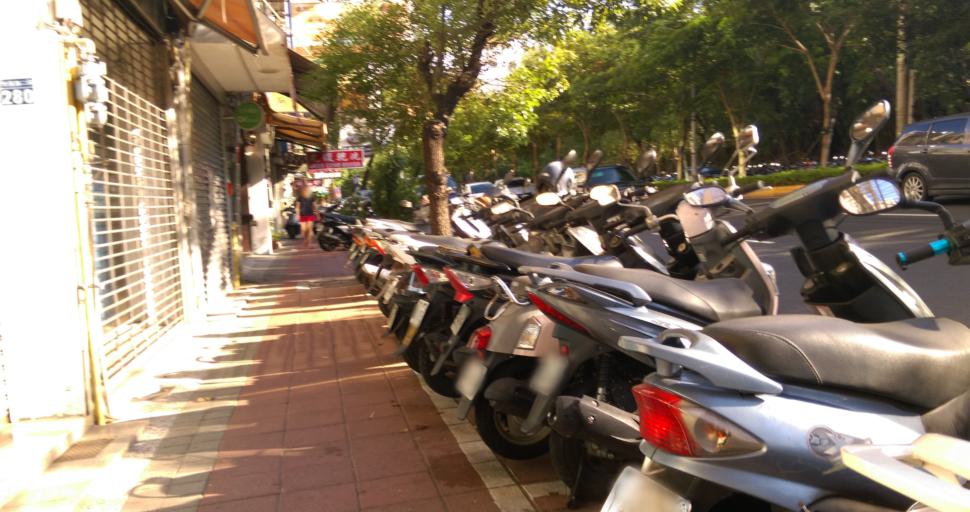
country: TW
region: Taiwan
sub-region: Hsinchu
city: Hsinchu
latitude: 24.7953
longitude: 120.9990
